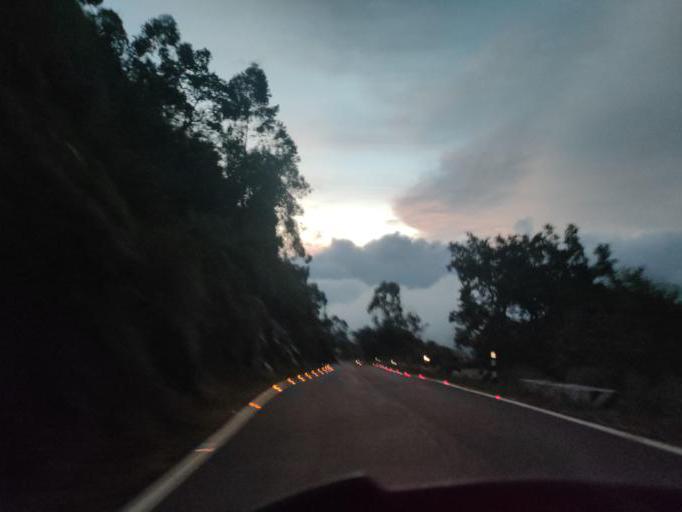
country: IN
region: Tamil Nadu
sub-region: Dindigul
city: Kodaikanal
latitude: 10.2817
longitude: 77.5351
